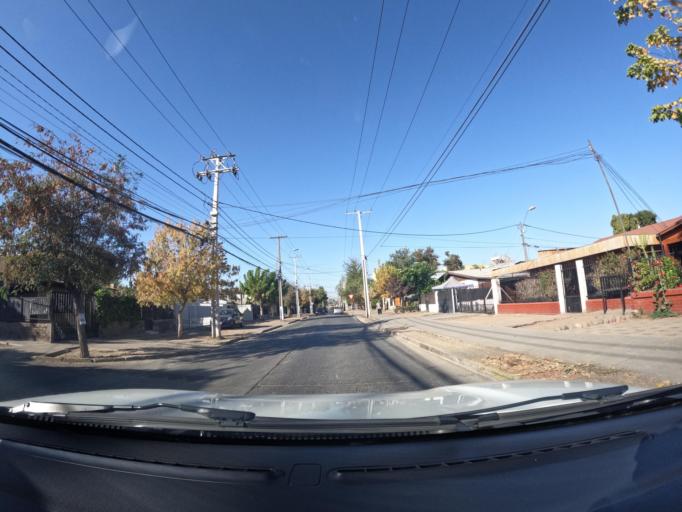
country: CL
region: Santiago Metropolitan
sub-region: Provincia de Santiago
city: Villa Presidente Frei, Nunoa, Santiago, Chile
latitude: -33.5078
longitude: -70.5754
